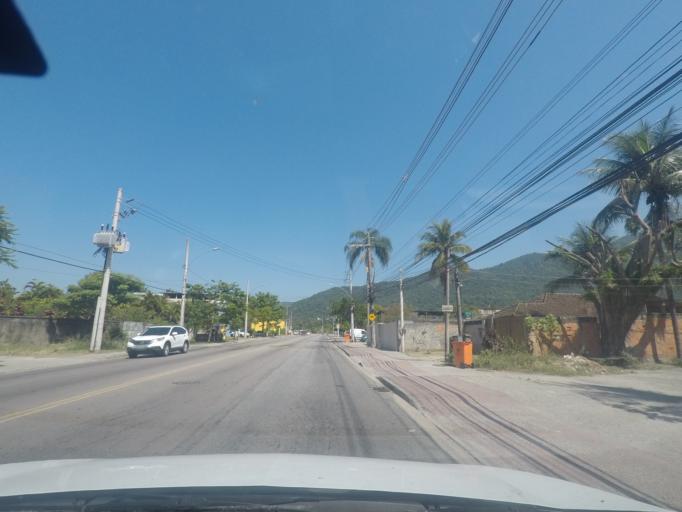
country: BR
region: Rio de Janeiro
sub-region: Nilopolis
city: Nilopolis
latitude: -22.9873
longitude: -43.4560
